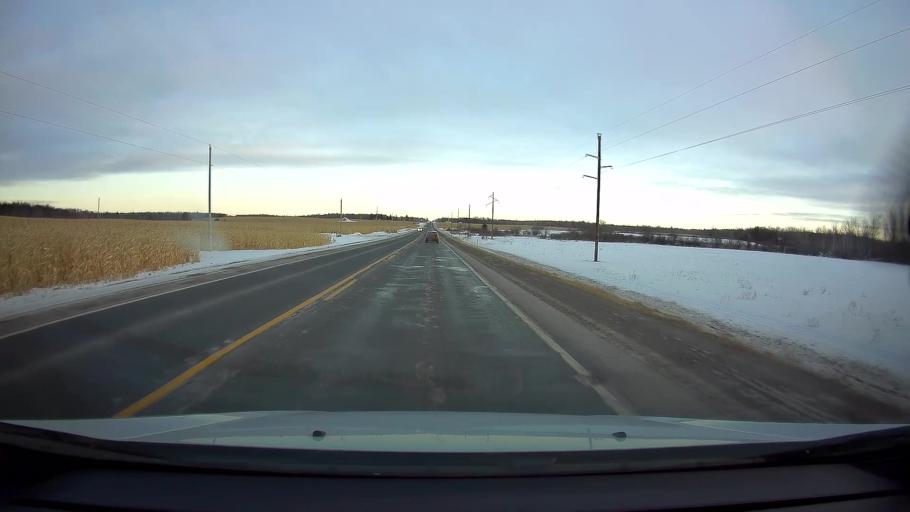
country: US
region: Wisconsin
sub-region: Barron County
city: Turtle Lake
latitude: 45.3423
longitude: -92.1667
